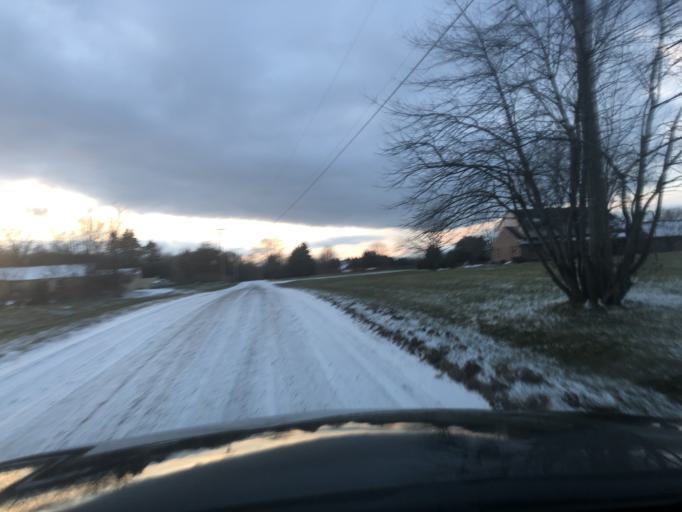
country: US
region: Michigan
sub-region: Oakland County
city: Milford
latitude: 42.5870
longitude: -83.6406
